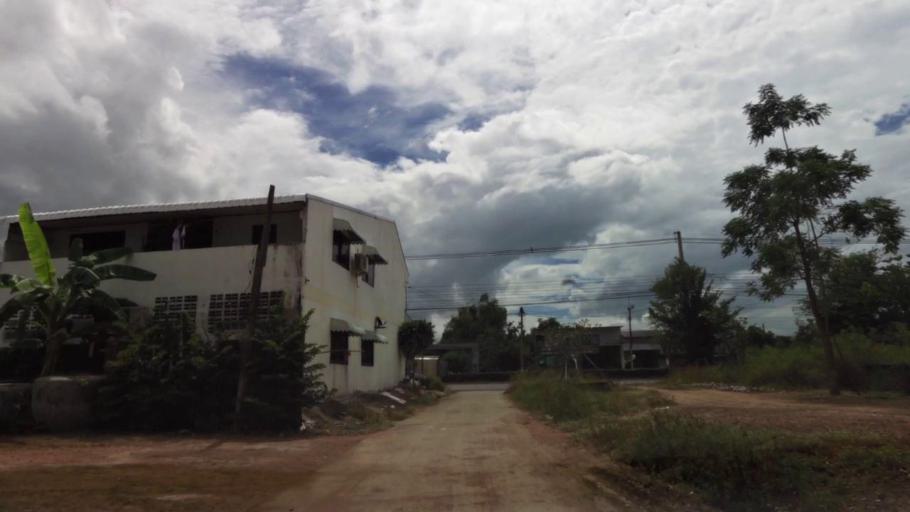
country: TH
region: Nakhon Sawan
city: Phai Sali
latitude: 15.5943
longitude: 100.6459
